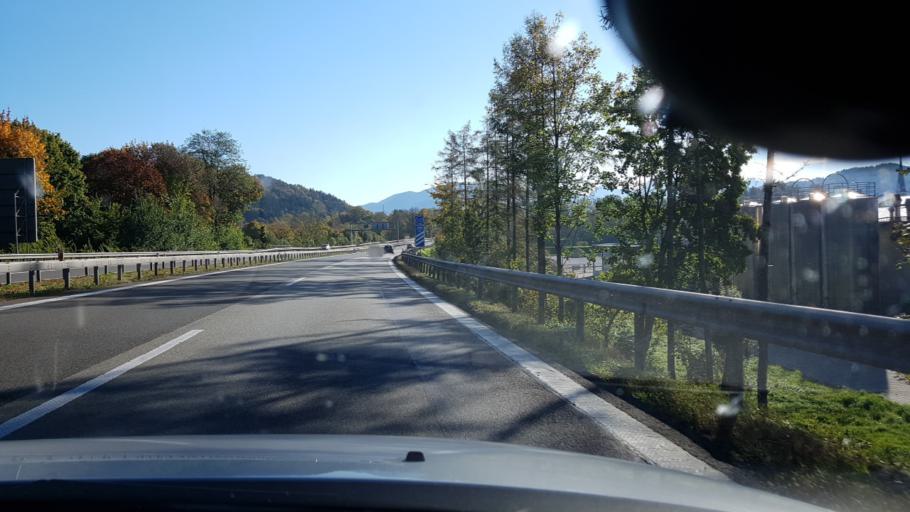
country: DE
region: Bavaria
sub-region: Upper Bavaria
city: Siegsdorf
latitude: 47.8287
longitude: 12.6403
